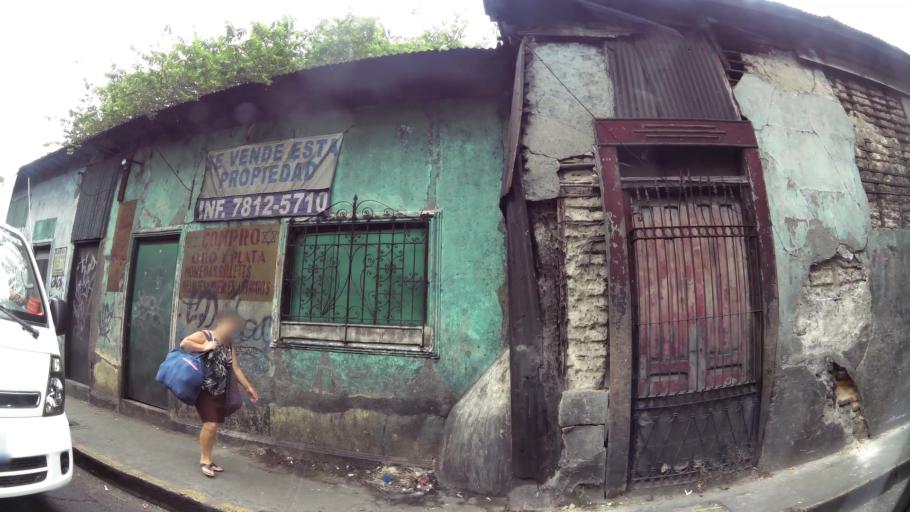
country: SV
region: San Salvador
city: San Salvador
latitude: 13.6994
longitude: -89.1867
